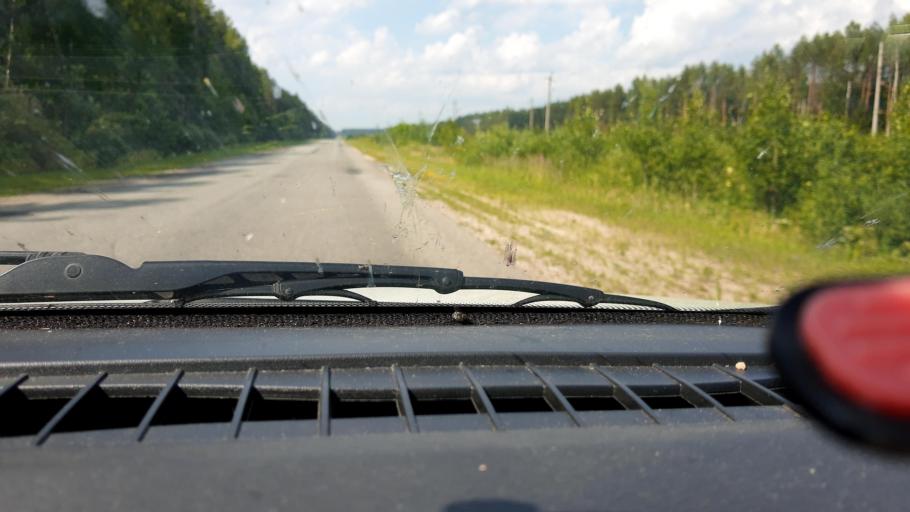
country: RU
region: Nizjnij Novgorod
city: Prudy
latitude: 57.4527
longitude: 46.0503
